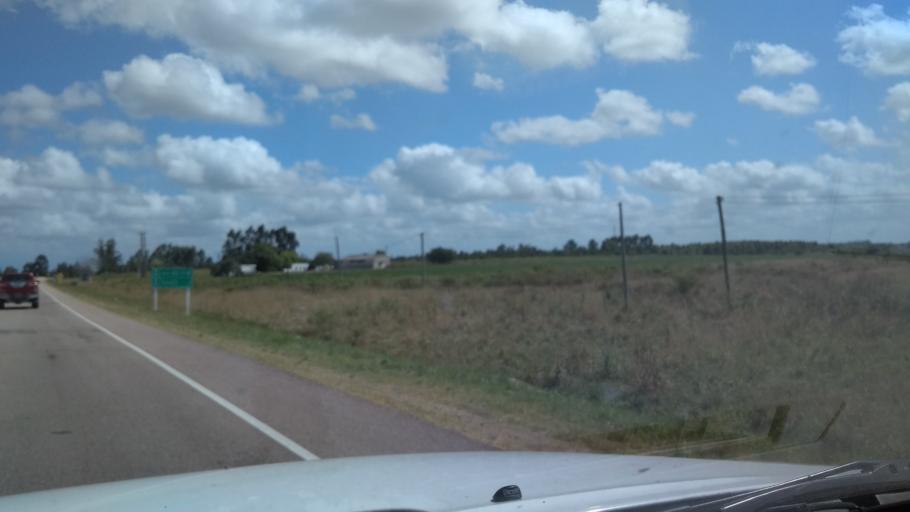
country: UY
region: Canelones
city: Sauce
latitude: -34.6348
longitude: -56.0522
